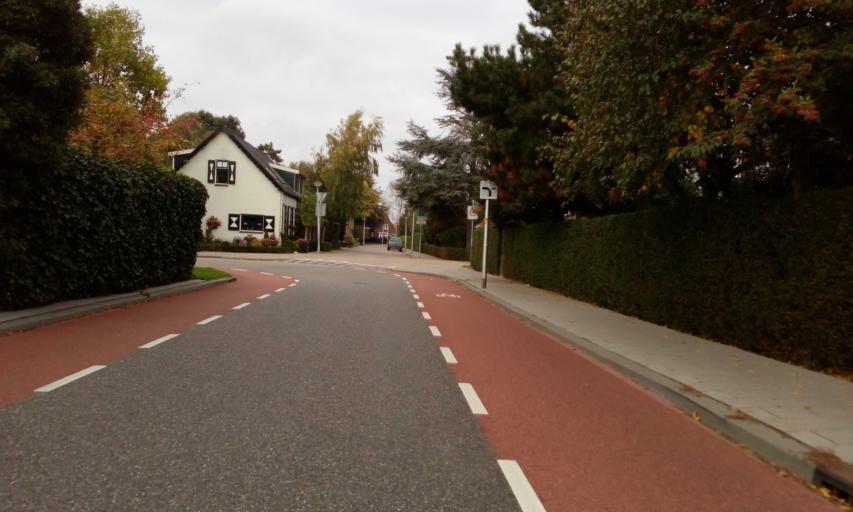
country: NL
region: South Holland
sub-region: Gemeente Albrandswaard
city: Rhoon
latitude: 51.8562
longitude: 4.4145
